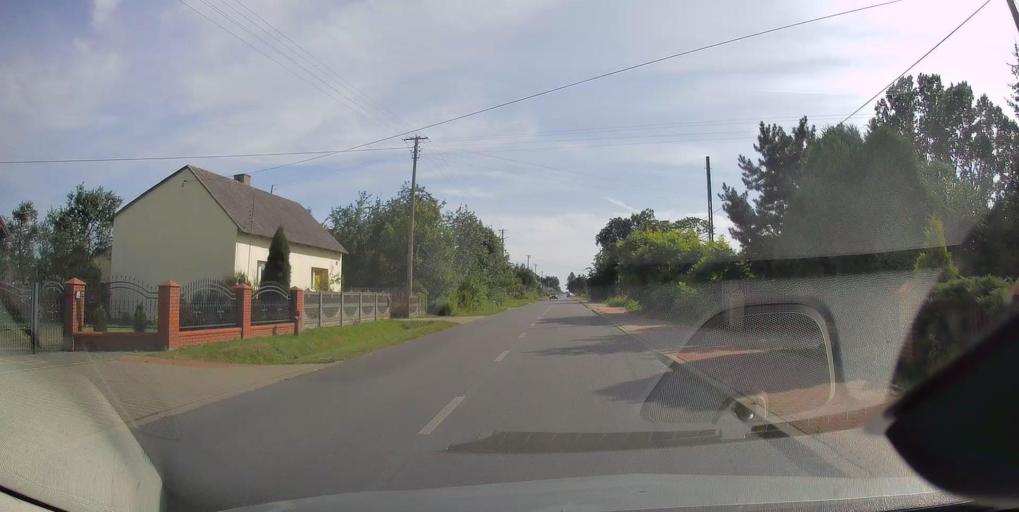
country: PL
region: Lodz Voivodeship
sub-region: Powiat opoczynski
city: Mniszkow
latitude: 51.4253
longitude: 20.0254
